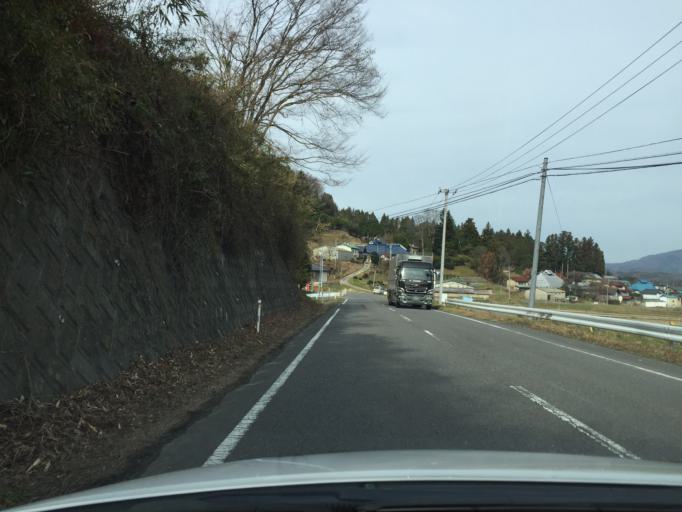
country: JP
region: Fukushima
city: Funehikimachi-funehiki
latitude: 37.4187
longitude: 140.5832
